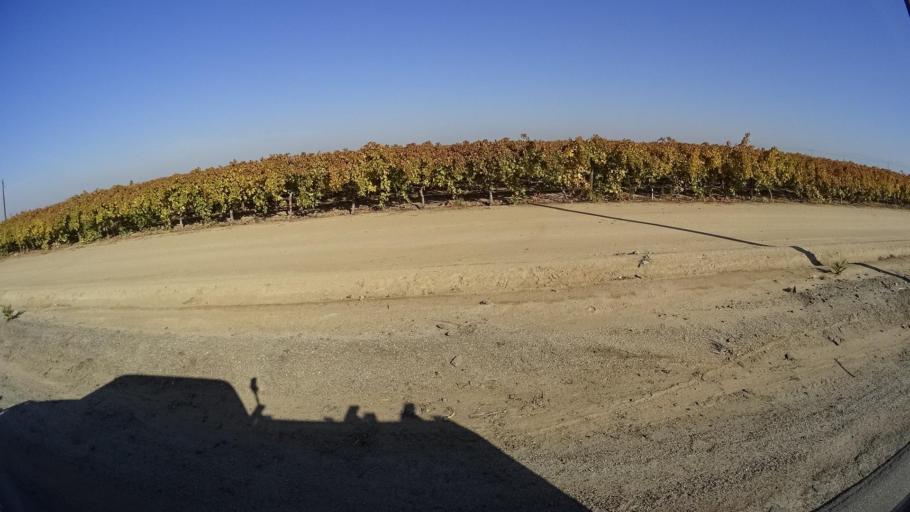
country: US
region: California
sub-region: Kern County
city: Delano
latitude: 35.7470
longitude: -119.1727
